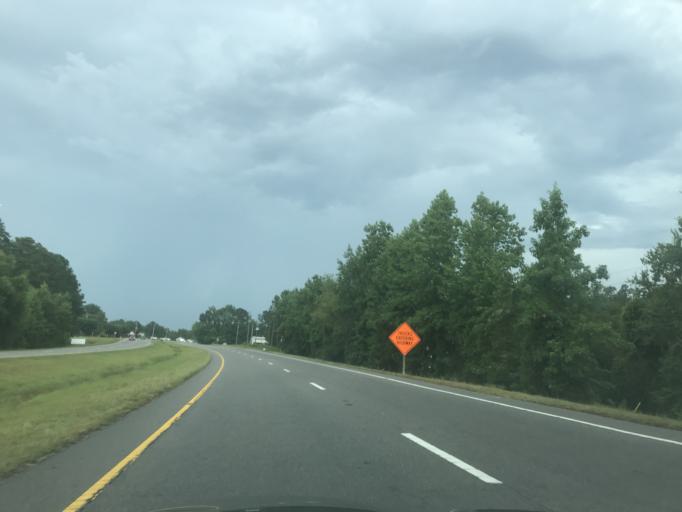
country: US
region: North Carolina
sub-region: Johnston County
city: Wilsons Mills
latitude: 35.5888
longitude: -78.4073
